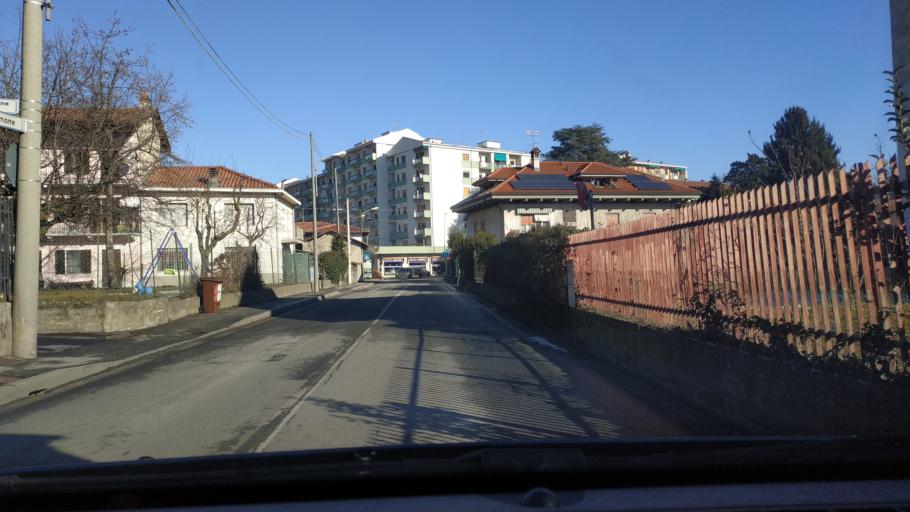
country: IT
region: Piedmont
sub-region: Provincia di Torino
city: Banchette
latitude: 45.4590
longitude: 7.8602
